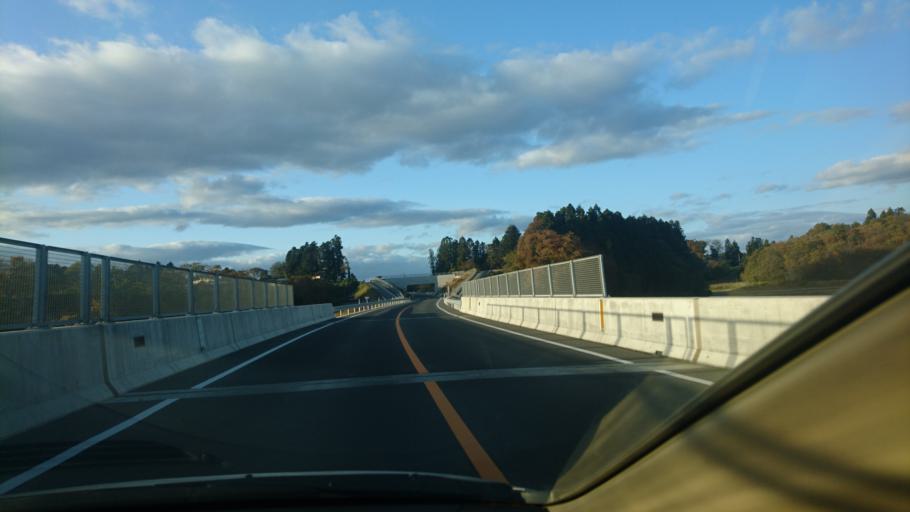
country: JP
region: Miyagi
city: Kogota
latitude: 38.7331
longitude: 141.0538
